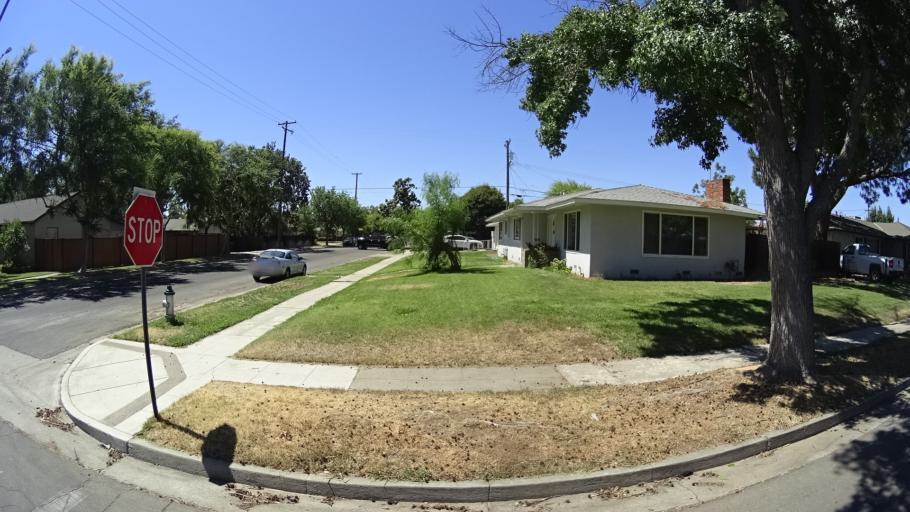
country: US
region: California
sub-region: Fresno County
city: Fresno
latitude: 36.7821
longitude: -119.8133
